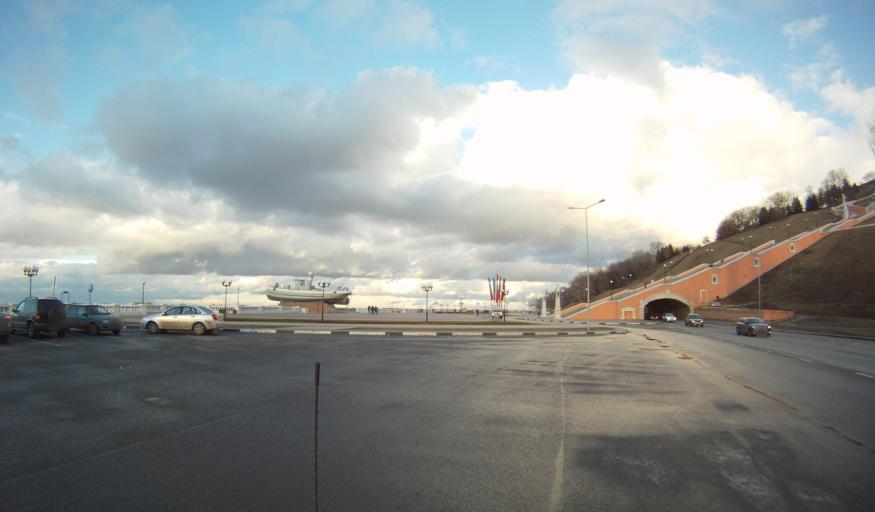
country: RU
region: Nizjnij Novgorod
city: Nizhniy Novgorod
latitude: 56.3319
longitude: 44.0081
